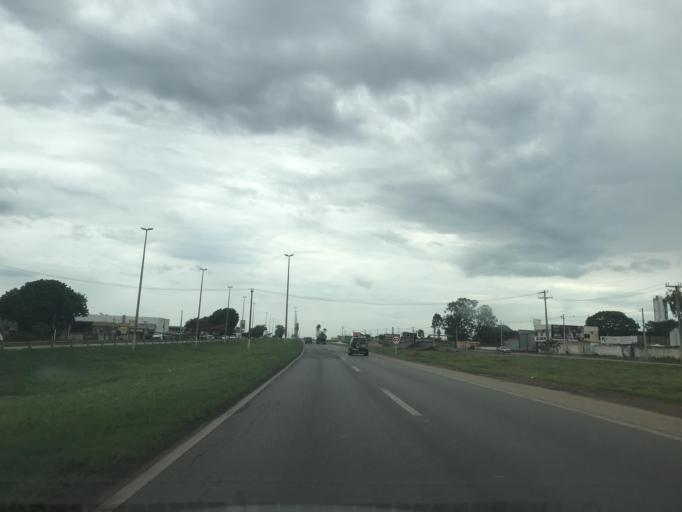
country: BR
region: Goias
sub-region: Luziania
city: Luziania
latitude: -16.1325
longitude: -47.9570
